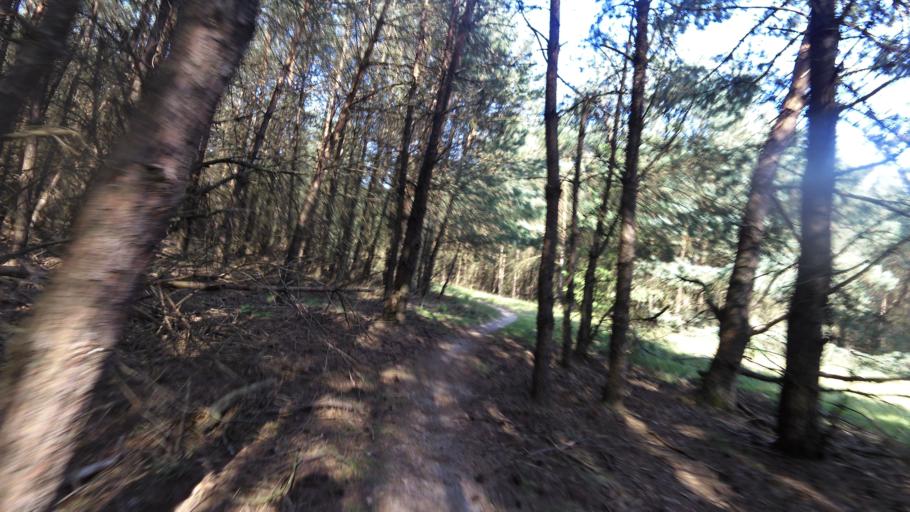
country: NL
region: Gelderland
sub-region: Gemeente Apeldoorn
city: Beekbergen
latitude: 52.1118
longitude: 5.9403
